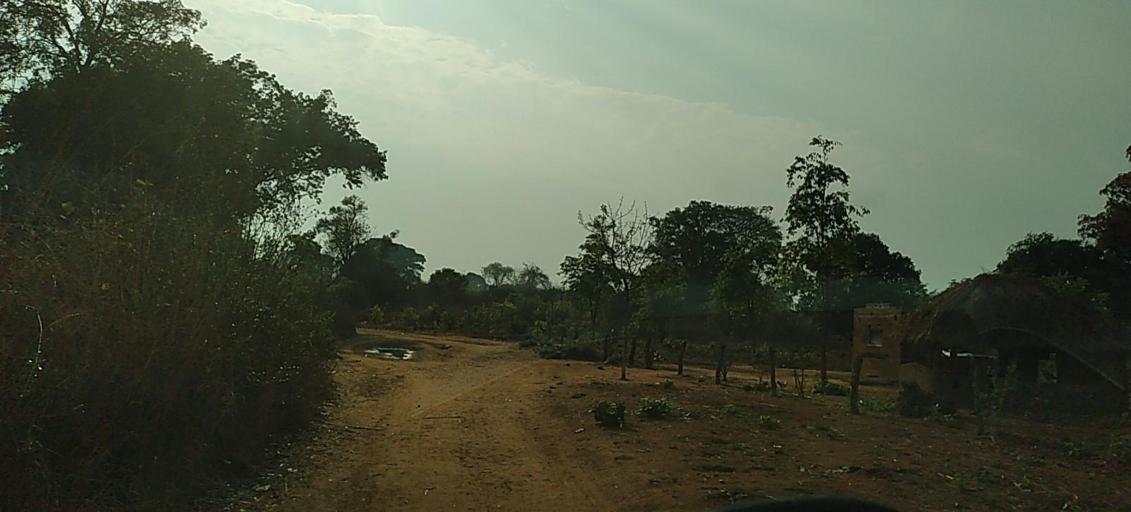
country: ZM
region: North-Western
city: Solwezi
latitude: -12.3534
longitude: 26.5336
